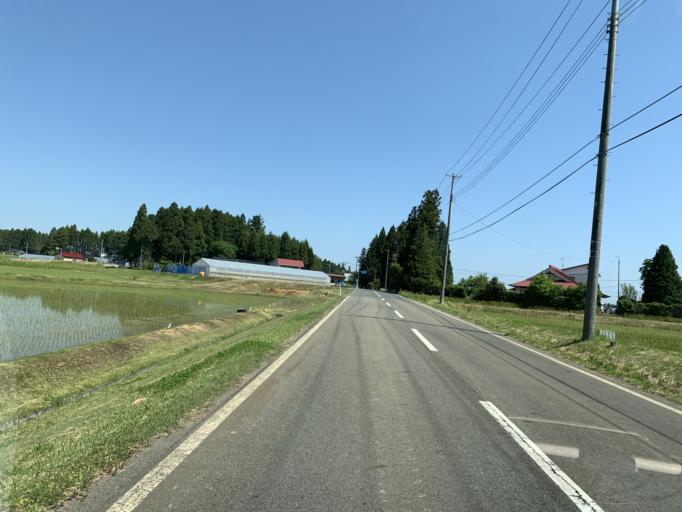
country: JP
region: Iwate
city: Mizusawa
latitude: 39.0709
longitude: 141.0638
